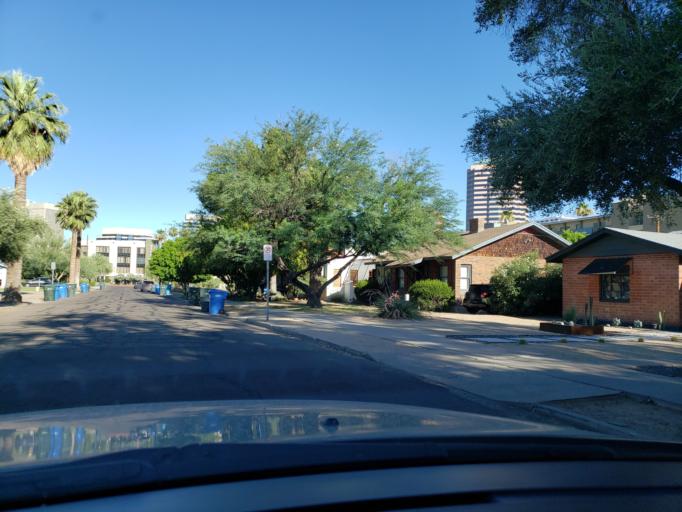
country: US
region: Arizona
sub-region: Maricopa County
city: Phoenix
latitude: 33.4780
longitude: -112.0674
